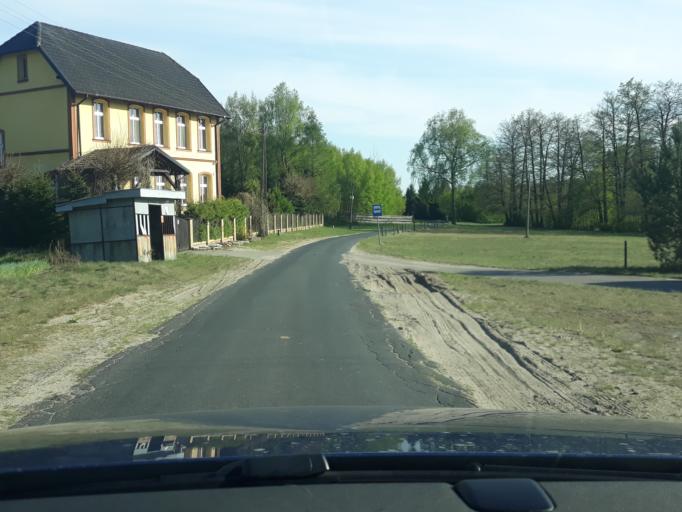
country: PL
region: Pomeranian Voivodeship
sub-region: Powiat czluchowski
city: Przechlewo
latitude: 53.8805
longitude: 17.3228
